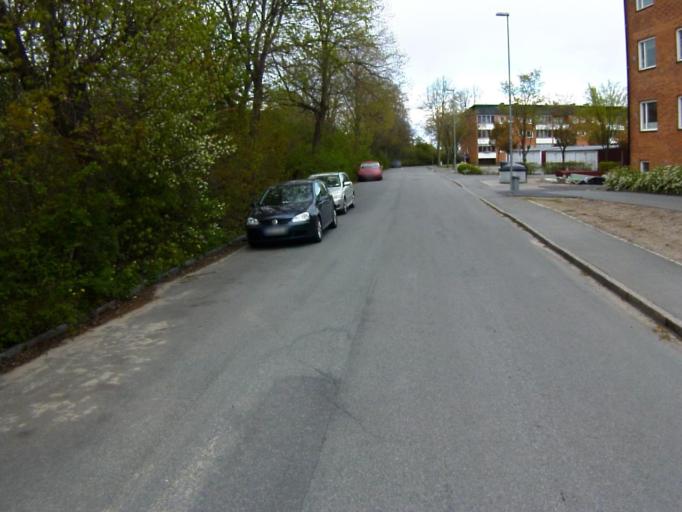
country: SE
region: Skane
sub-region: Kristianstads Kommun
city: Kristianstad
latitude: 56.0471
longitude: 14.1650
